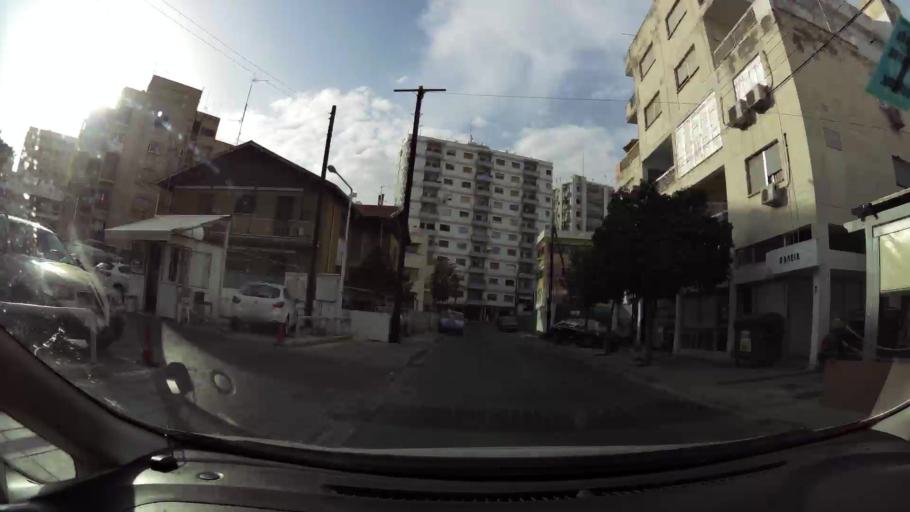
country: CY
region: Lefkosia
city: Nicosia
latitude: 35.1646
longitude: 33.3606
